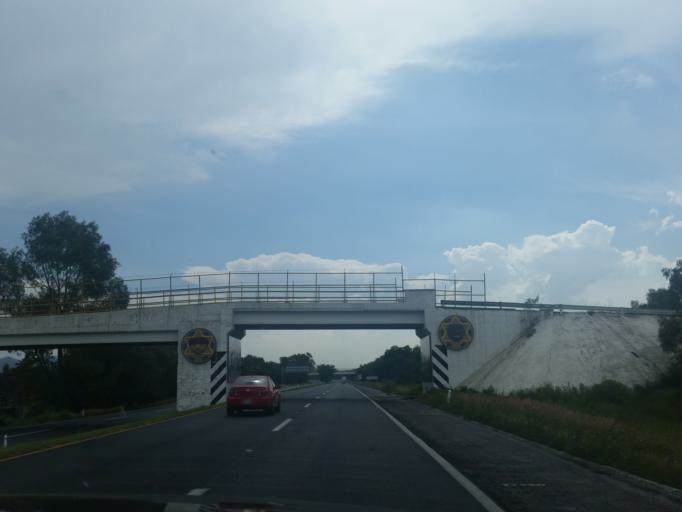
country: MX
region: Mexico
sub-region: Acolman de Nezahualcoyotl
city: Prados de San Juan
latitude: 19.6198
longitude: -98.9554
